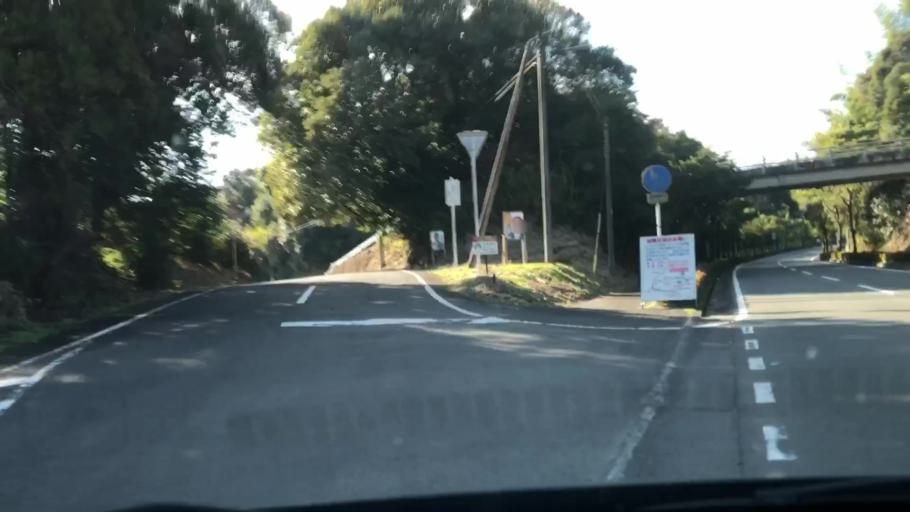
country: JP
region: Kagoshima
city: Satsumasendai
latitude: 31.8584
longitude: 130.3658
